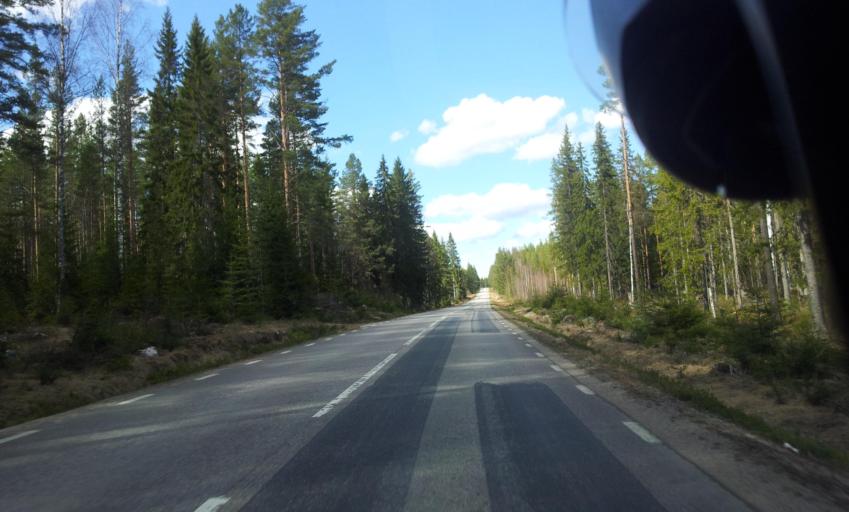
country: SE
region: Gaevleborg
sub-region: Ovanakers Kommun
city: Edsbyn
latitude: 61.3405
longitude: 15.8223
